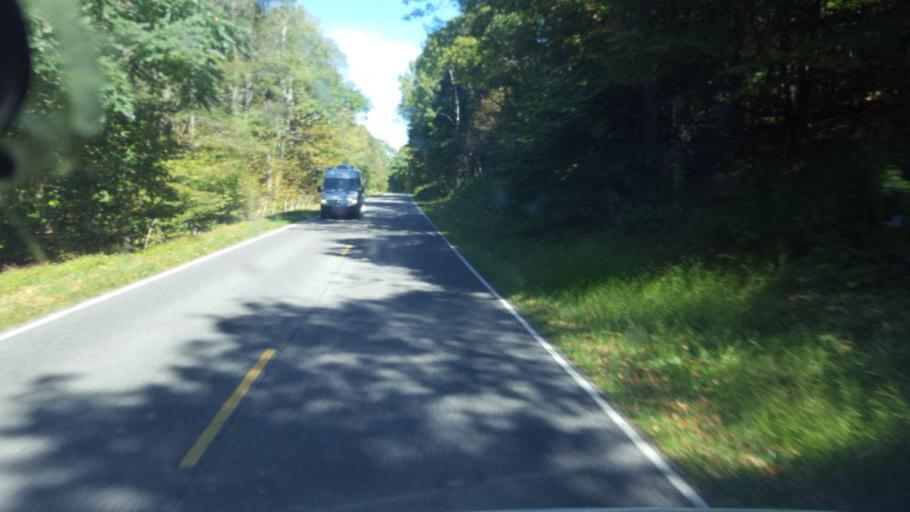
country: US
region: Virginia
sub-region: Page County
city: Stanley
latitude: 38.4825
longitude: -78.4541
